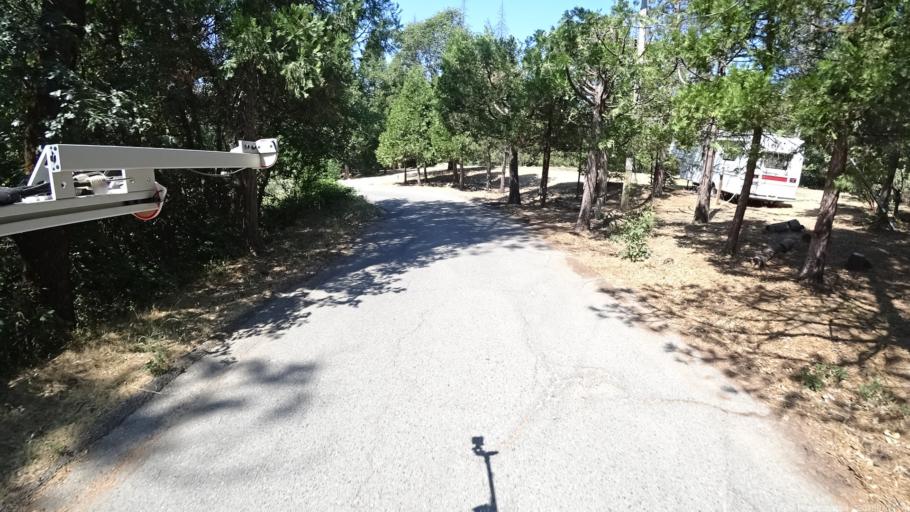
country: US
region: California
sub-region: Fresno County
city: Auberry
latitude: 37.2314
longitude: -119.4563
